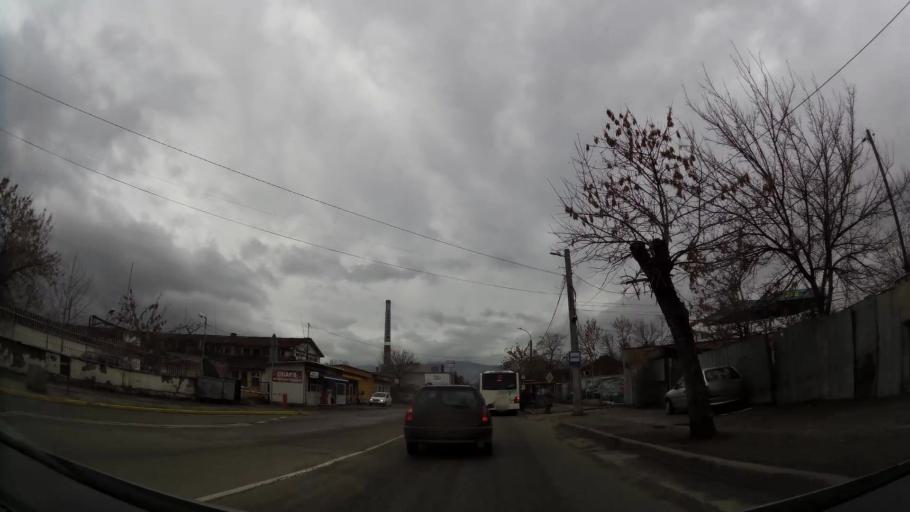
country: BG
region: Sofia-Capital
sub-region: Stolichna Obshtina
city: Sofia
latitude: 42.7249
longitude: 23.2815
